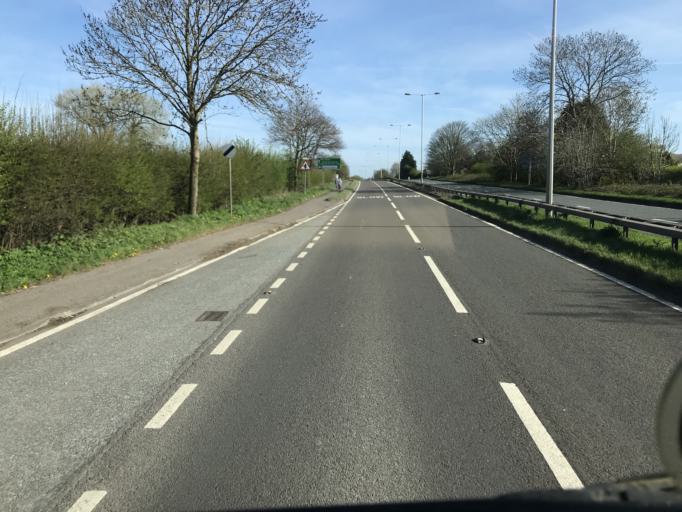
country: GB
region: England
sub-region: Cheshire West and Chester
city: Marston
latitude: 53.2586
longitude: -2.4618
